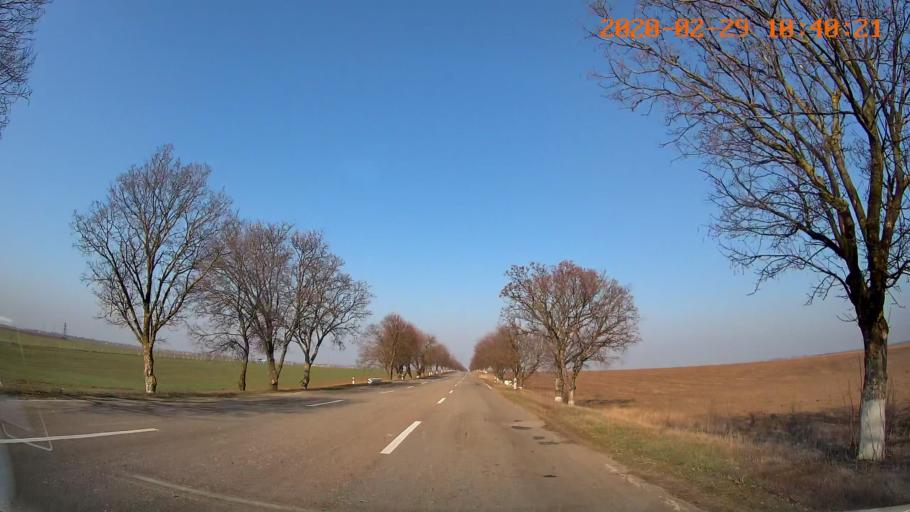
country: MD
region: Anenii Noi
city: Varnita
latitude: 47.0322
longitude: 29.4410
